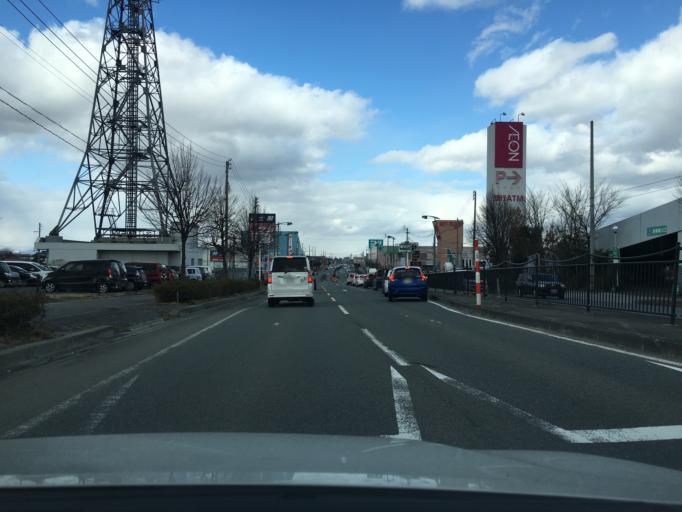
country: JP
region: Yamagata
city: Yamagata-shi
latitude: 38.2270
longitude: 140.3037
